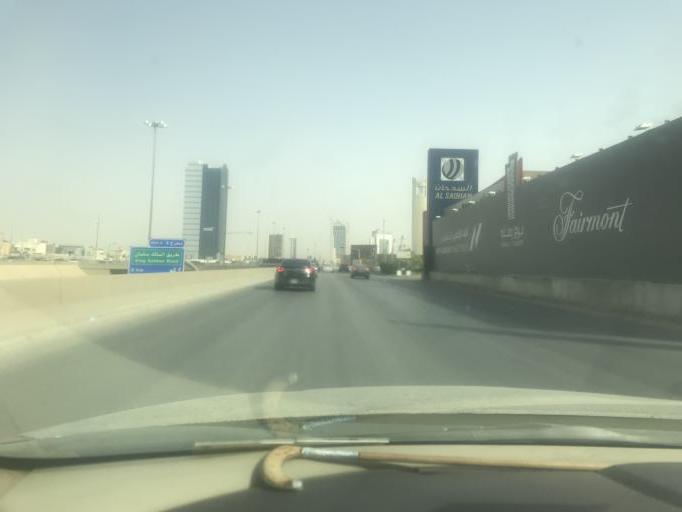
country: SA
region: Ar Riyad
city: Riyadh
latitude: 24.8086
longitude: 46.6234
